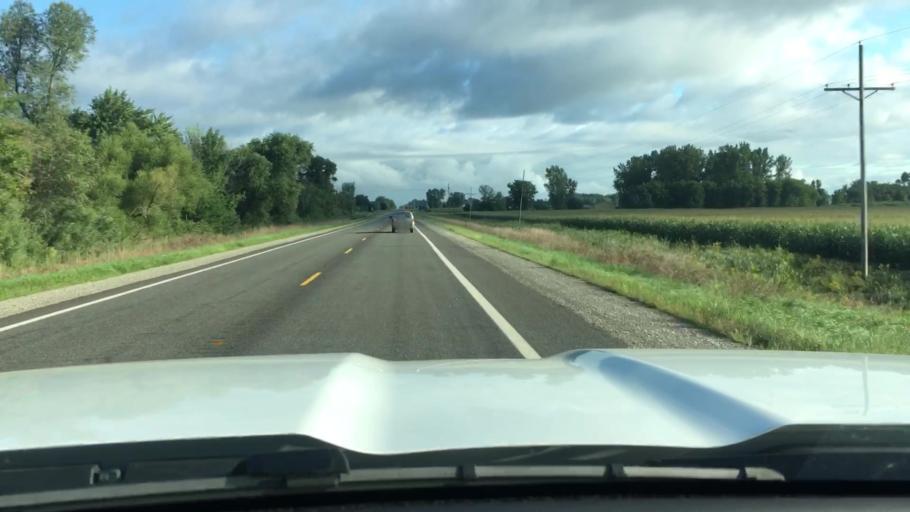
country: US
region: Michigan
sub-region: Tuscola County
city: Caro
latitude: 43.3766
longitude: -83.3832
